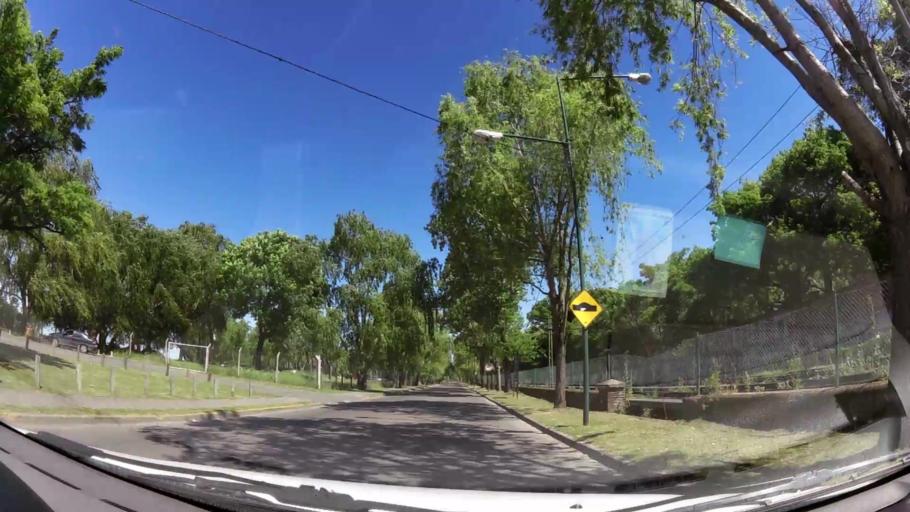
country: AR
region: Buenos Aires
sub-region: Partido de Vicente Lopez
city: Olivos
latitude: -34.4814
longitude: -58.4826
